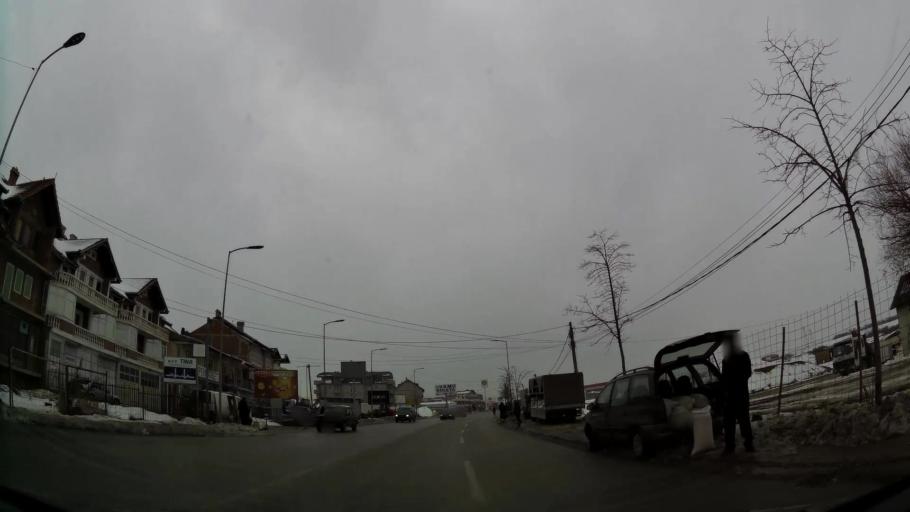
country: XK
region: Pristina
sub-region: Komuna e Prishtines
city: Pristina
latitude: 42.6999
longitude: 21.1591
